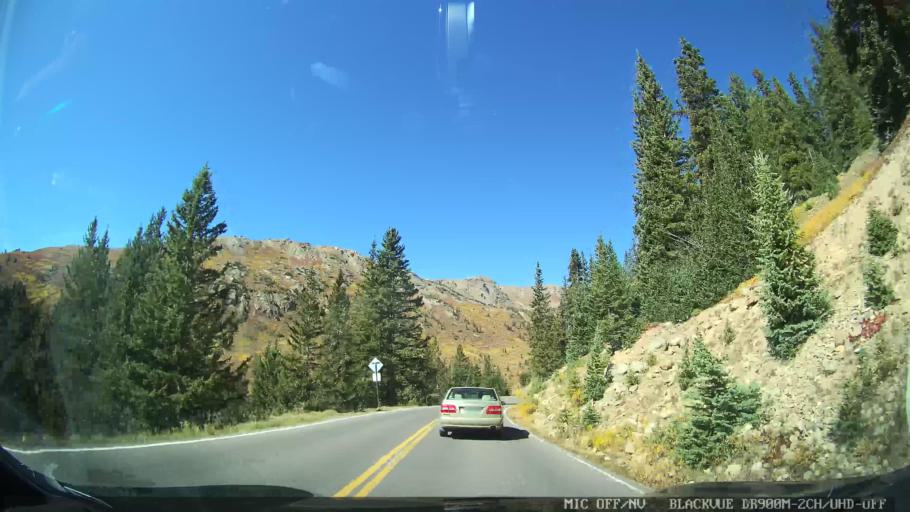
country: US
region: Colorado
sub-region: Pitkin County
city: Aspen
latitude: 39.1209
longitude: -106.5758
